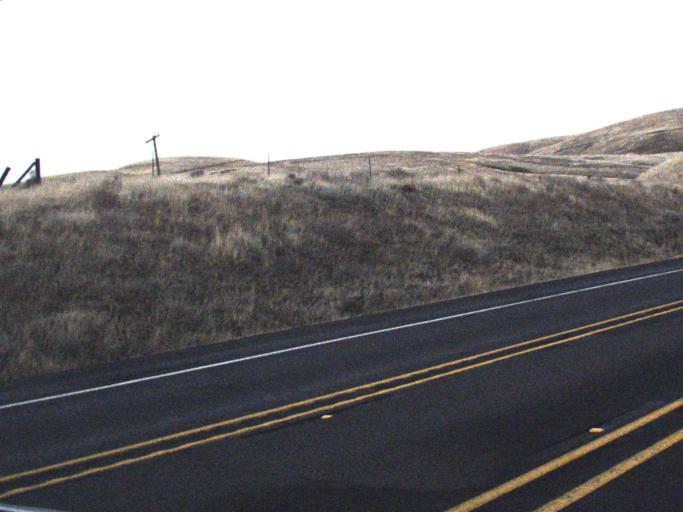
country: US
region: Washington
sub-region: Columbia County
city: Dayton
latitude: 46.5088
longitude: -117.9729
